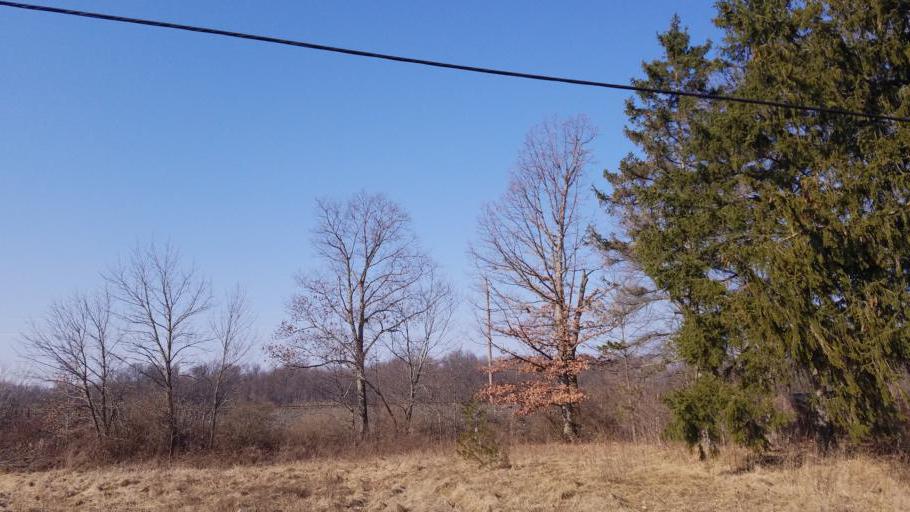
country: US
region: Ohio
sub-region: Crawford County
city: Galion
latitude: 40.7069
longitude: -82.7932
